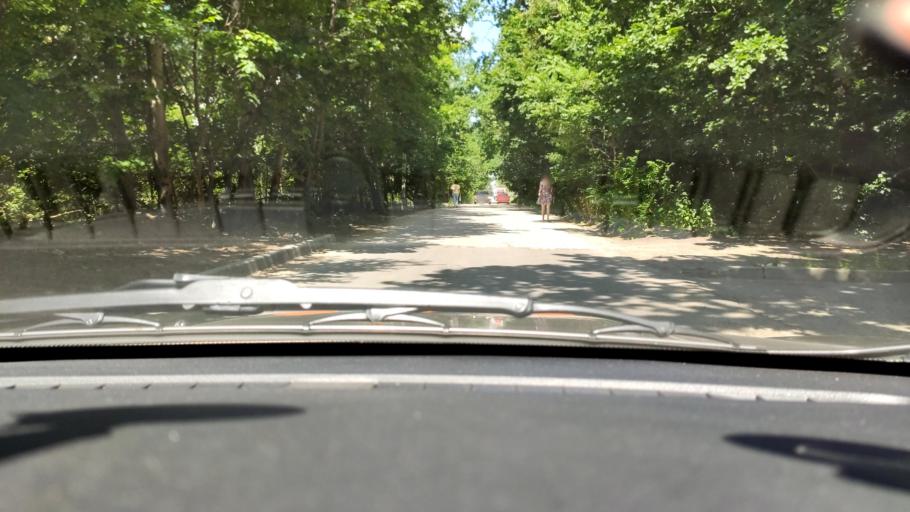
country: RU
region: Voronezj
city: Podgornoye
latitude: 51.7284
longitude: 39.1915
